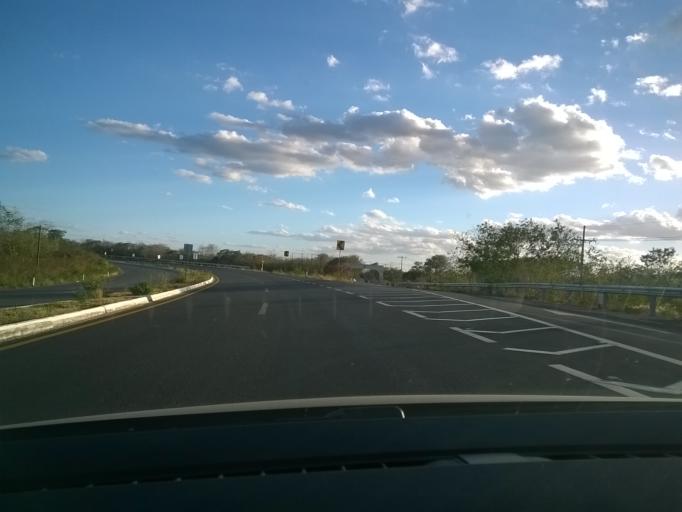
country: MX
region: Yucatan
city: Tekoh
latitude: 20.7631
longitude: -89.4688
